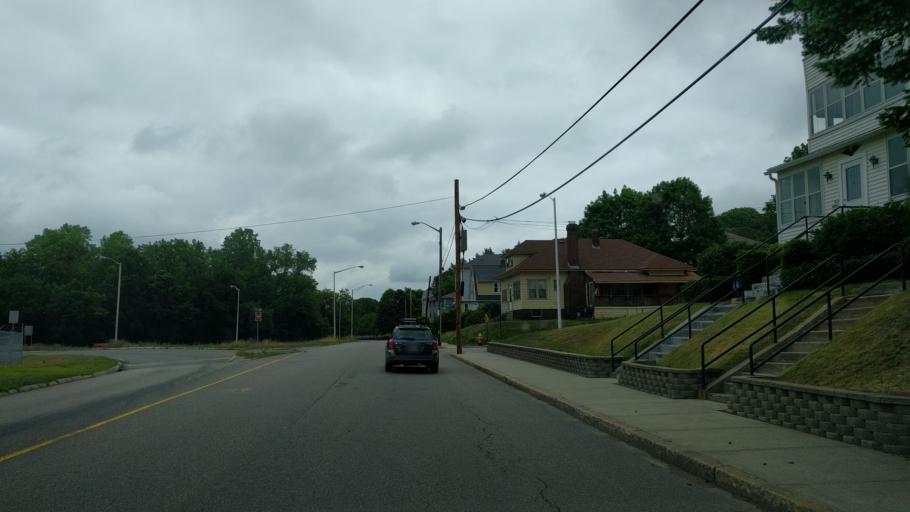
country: US
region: Massachusetts
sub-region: Worcester County
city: Worcester
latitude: 42.2363
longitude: -71.8157
